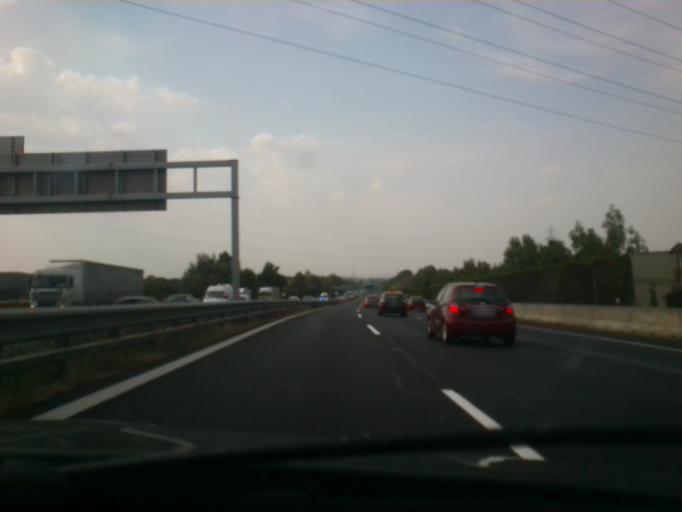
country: CZ
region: Central Bohemia
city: Velke Popovice
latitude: 49.9485
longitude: 14.6456
